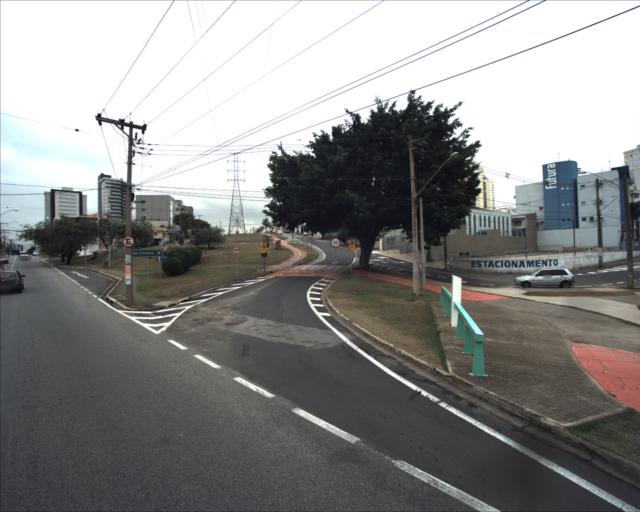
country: BR
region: Sao Paulo
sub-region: Sorocaba
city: Sorocaba
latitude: -23.5156
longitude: -47.4652
